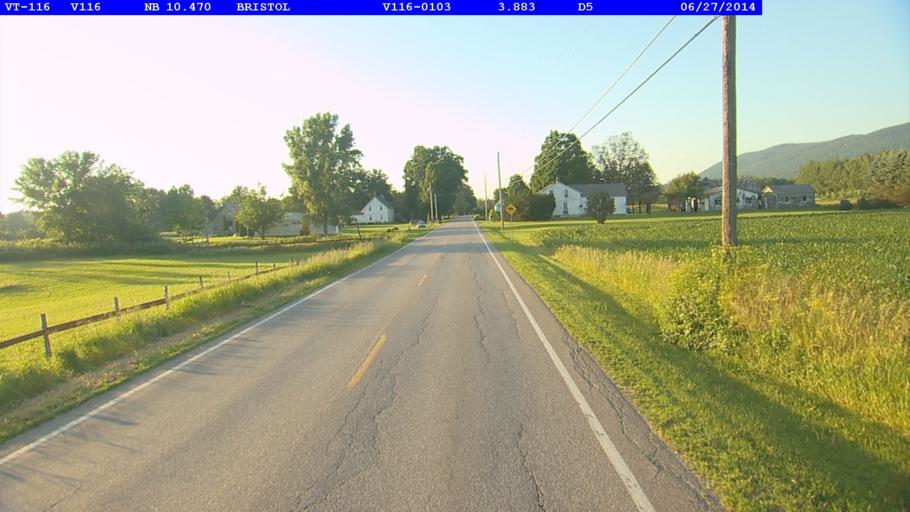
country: US
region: Vermont
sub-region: Addison County
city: Bristol
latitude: 44.1064
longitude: -73.0969
